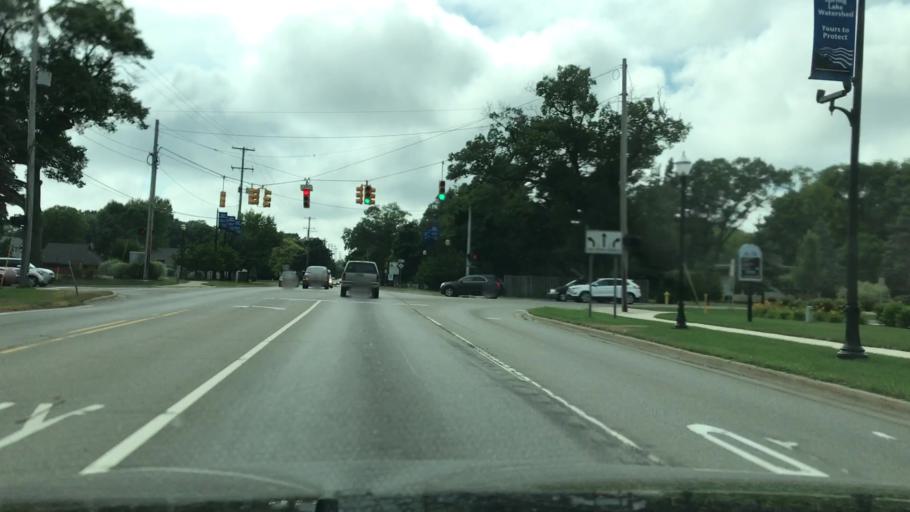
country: US
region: Michigan
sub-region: Ottawa County
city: Spring Lake
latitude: 43.0767
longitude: -86.1759
